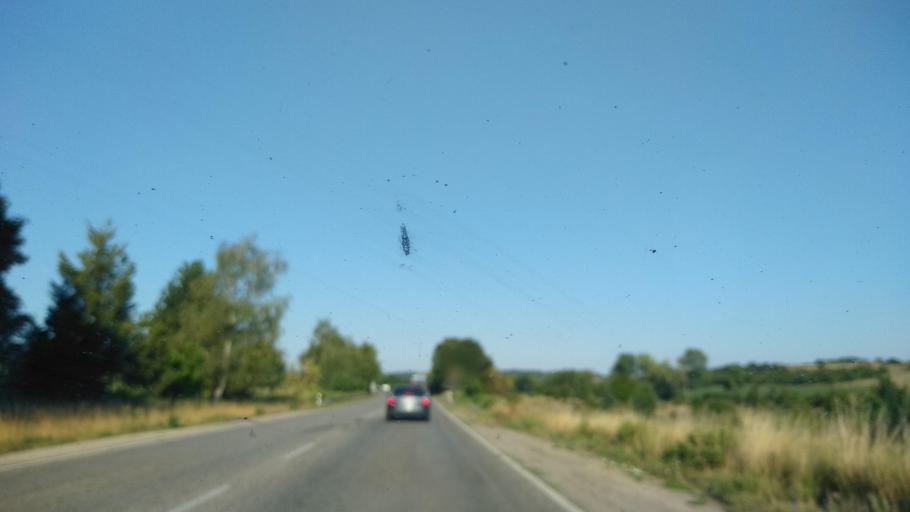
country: BG
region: Veliko Turnovo
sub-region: Obshtina Pavlikeni
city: Byala Cherkva
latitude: 43.0840
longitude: 25.3579
